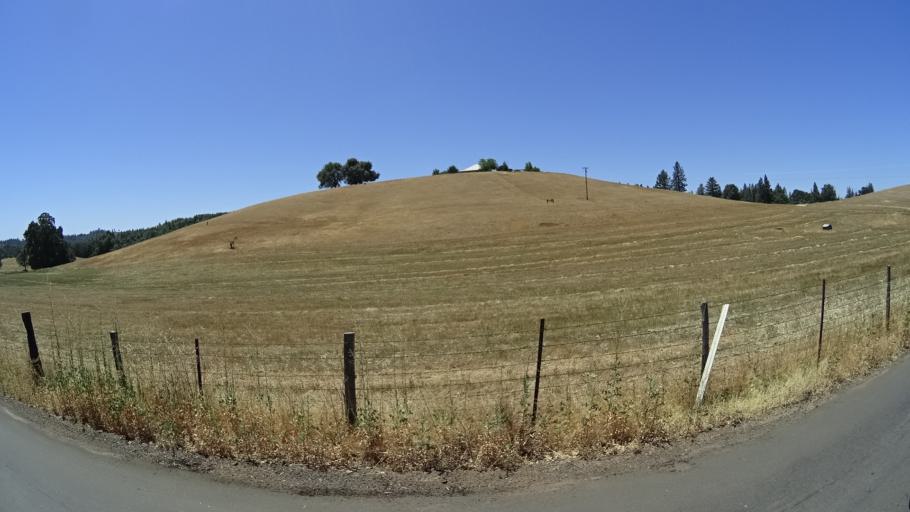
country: US
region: California
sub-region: Calaveras County
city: Mountain Ranch
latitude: 38.2325
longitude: -120.5509
